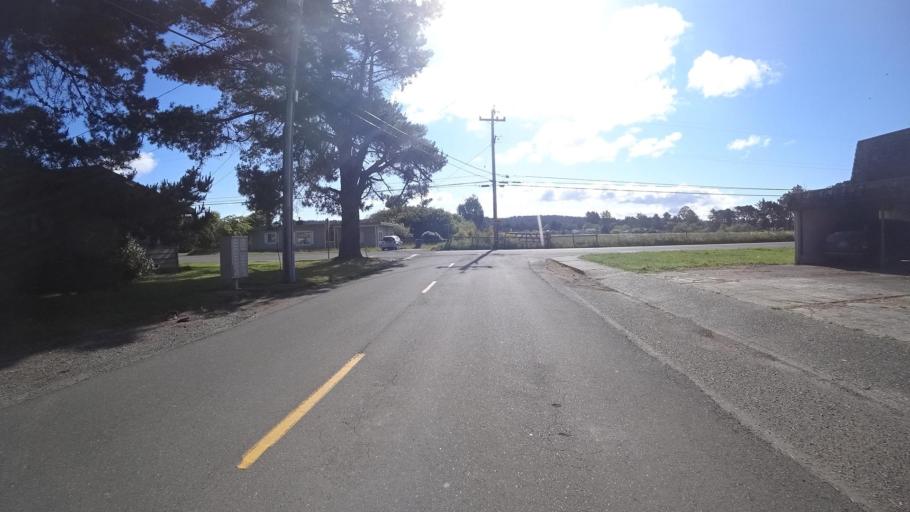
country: US
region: California
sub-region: Humboldt County
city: McKinleyville
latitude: 40.9598
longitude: -124.1108
